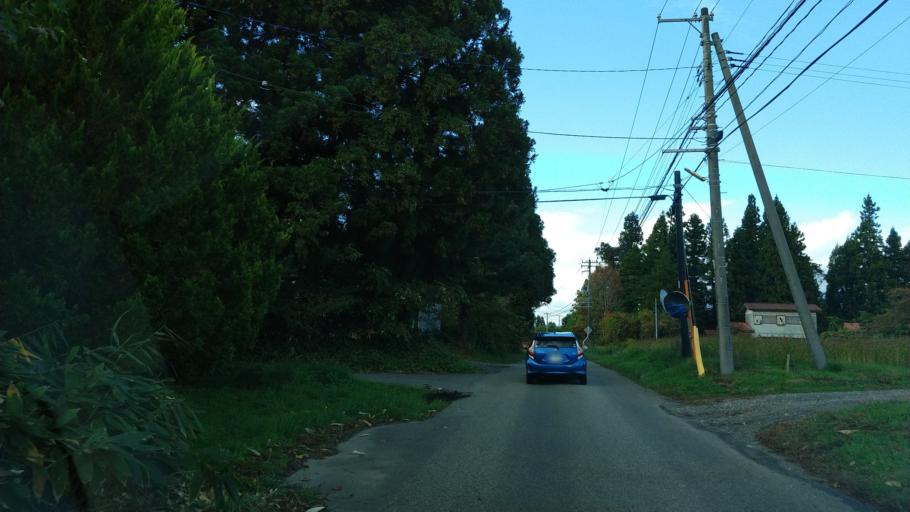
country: JP
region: Fukushima
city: Inawashiro
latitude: 37.5208
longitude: 140.0129
